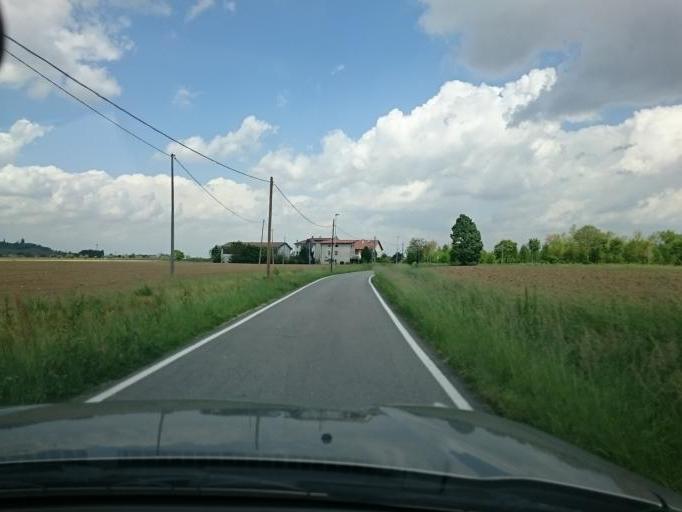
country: IT
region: Veneto
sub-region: Provincia di Vicenza
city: Villaganzerla
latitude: 45.4553
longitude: 11.6198
